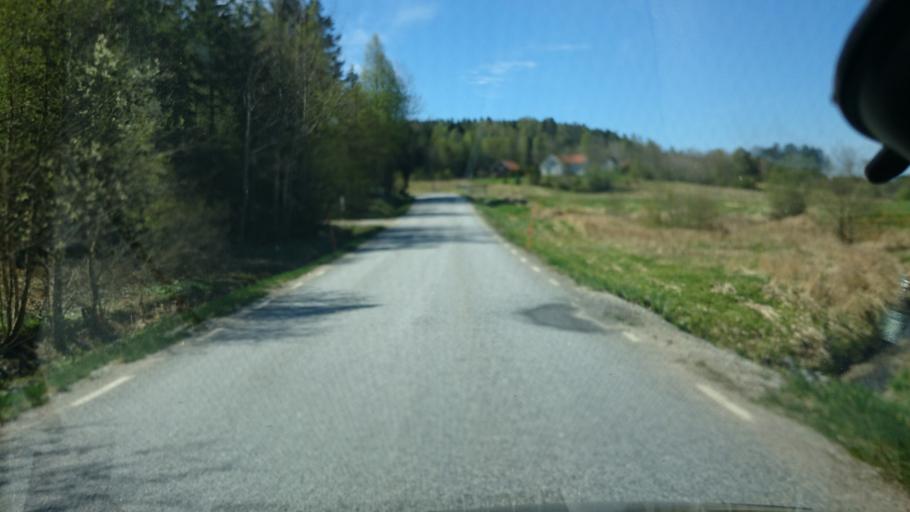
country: SE
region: Vaestra Goetaland
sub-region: Munkedals Kommun
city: Munkedal
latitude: 58.4134
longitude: 11.6773
